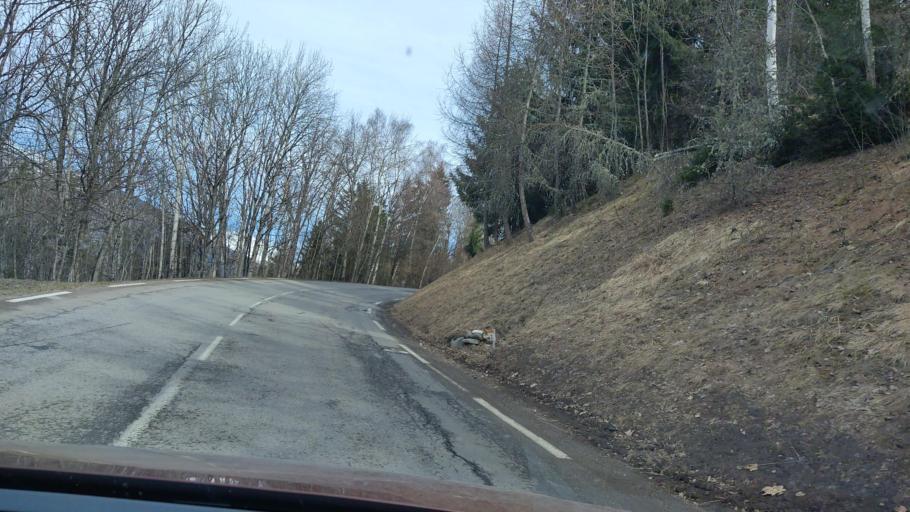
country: FR
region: Rhone-Alpes
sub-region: Departement de la Savoie
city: Macot-la-Plagne
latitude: 45.5459
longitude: 6.6667
